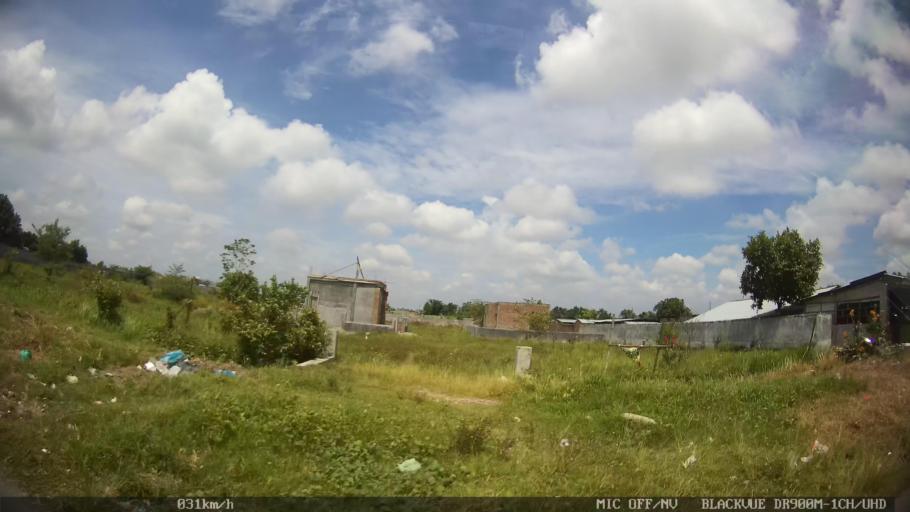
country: ID
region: North Sumatra
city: Percut
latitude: 3.6179
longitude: 98.7815
